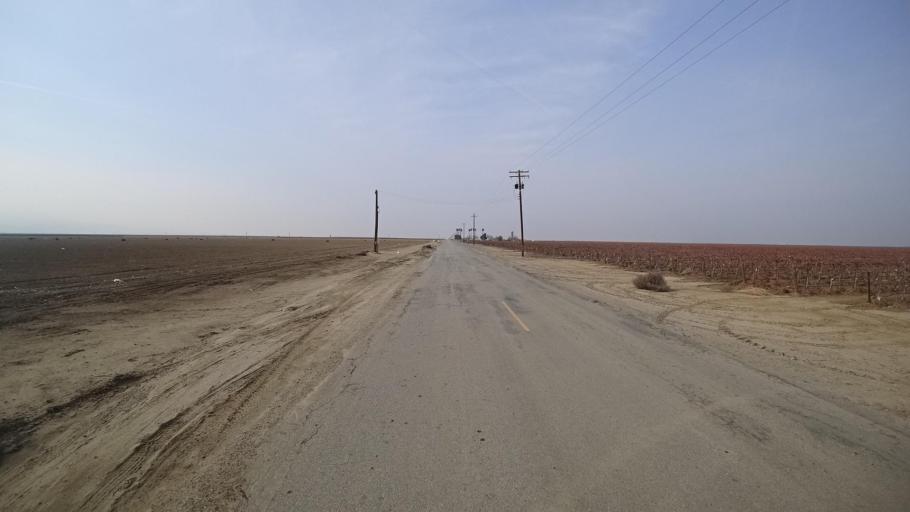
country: US
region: California
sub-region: Kern County
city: Greenfield
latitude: 35.0766
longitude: -119.0743
